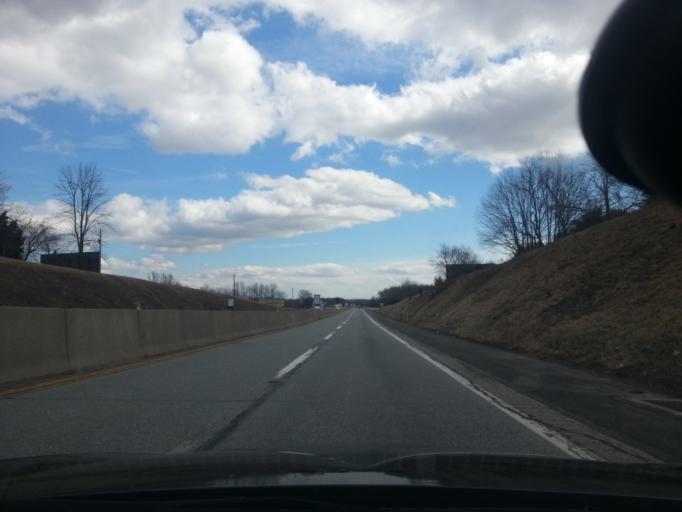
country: US
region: Pennsylvania
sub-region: Bucks County
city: Spinnerstown
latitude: 40.4521
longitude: -75.4378
